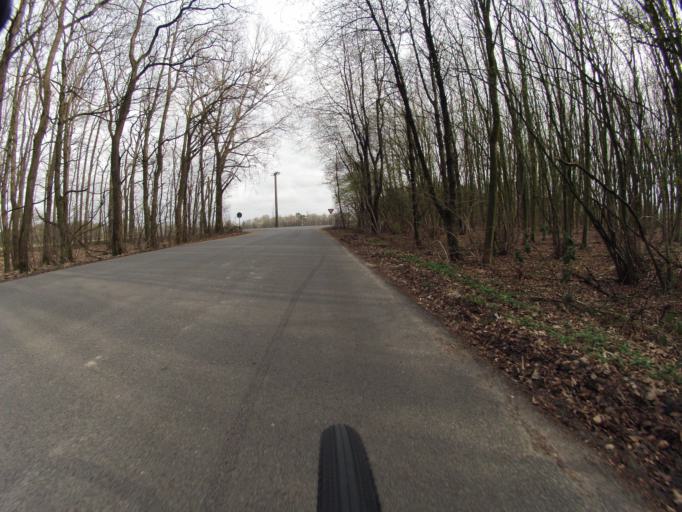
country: DE
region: North Rhine-Westphalia
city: Ibbenburen
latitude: 52.3187
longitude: 7.6961
